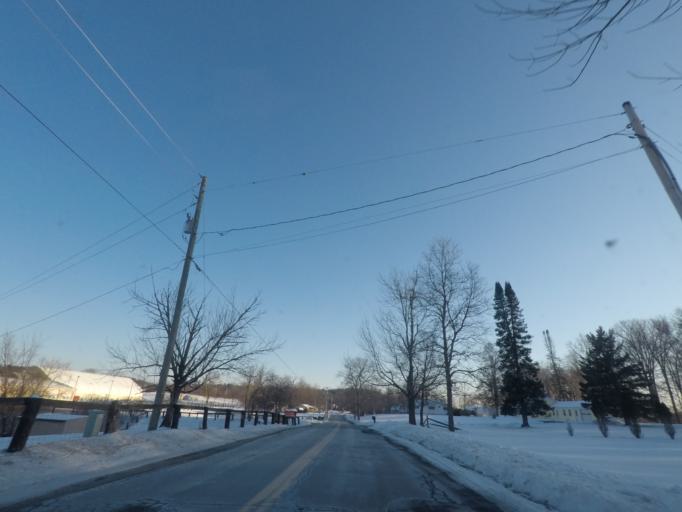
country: US
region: New York
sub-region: Saratoga County
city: Mechanicville
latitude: 42.8822
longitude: -73.6733
